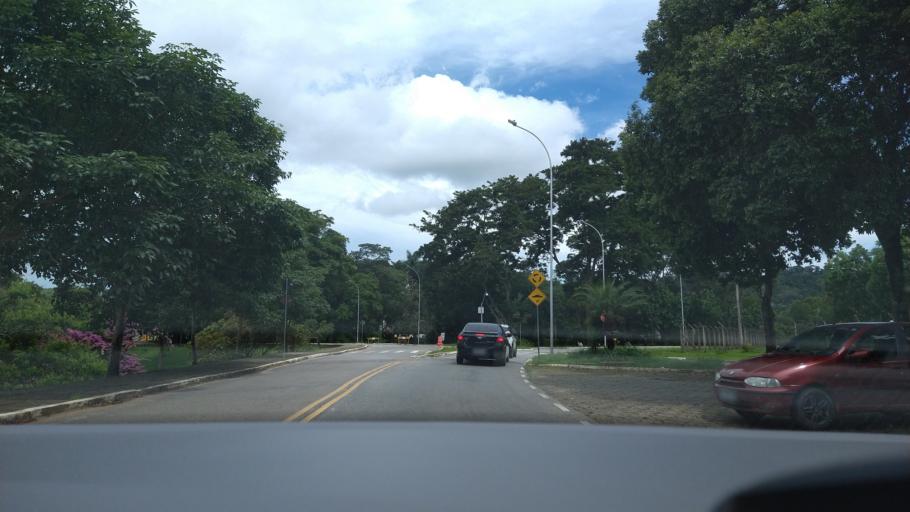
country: BR
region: Minas Gerais
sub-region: Vicosa
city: Vicosa
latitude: -20.7601
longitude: -42.8722
